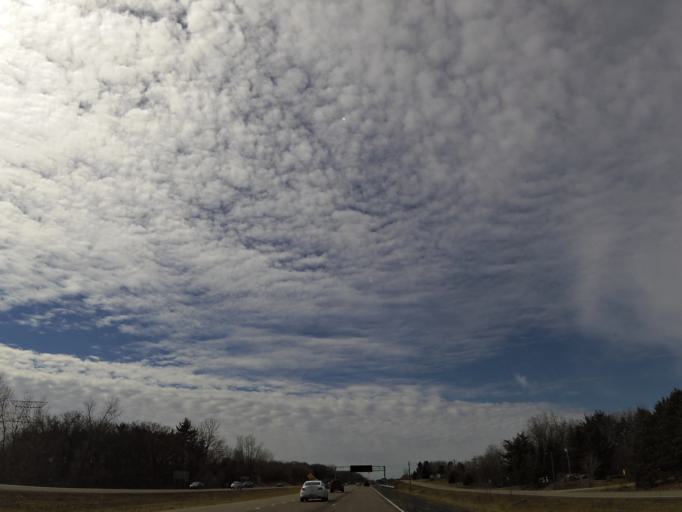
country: US
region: Minnesota
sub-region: Washington County
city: Mahtomedi
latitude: 45.0358
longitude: -92.9321
